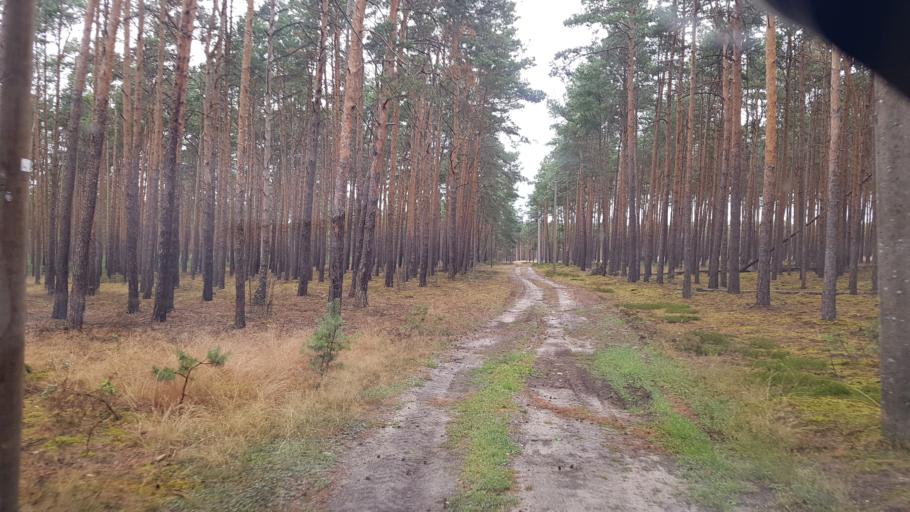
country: DE
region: Brandenburg
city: Schilda
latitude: 51.6392
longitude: 13.3520
